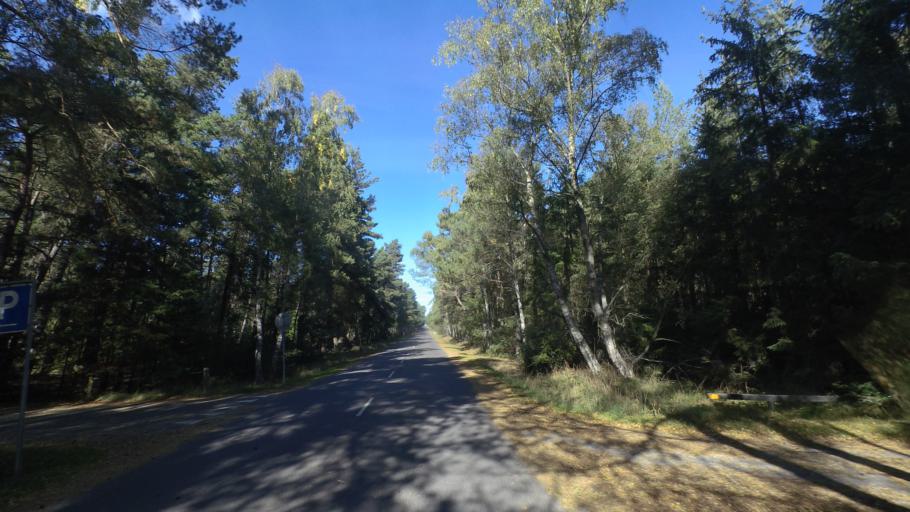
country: DK
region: Capital Region
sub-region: Bornholm Kommune
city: Nexo
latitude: 54.9944
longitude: 15.0777
